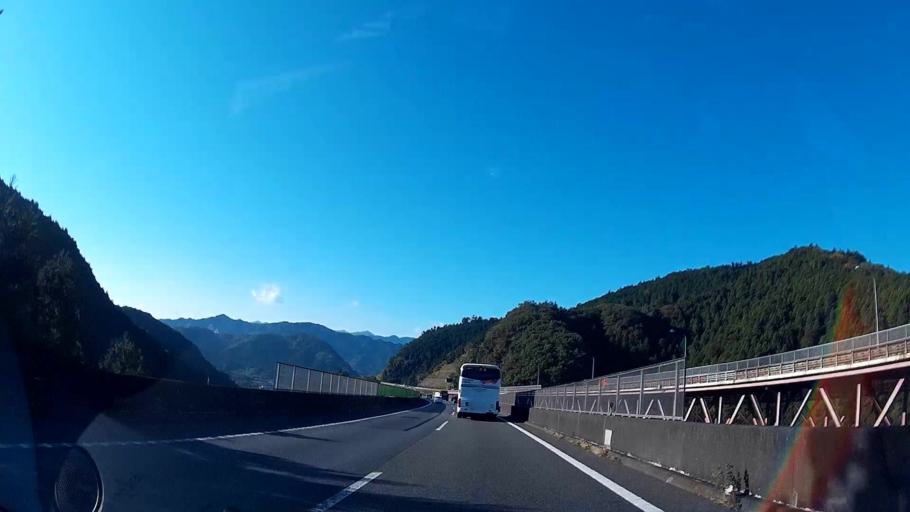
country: JP
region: Yamanashi
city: Uenohara
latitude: 35.6321
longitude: 139.2049
